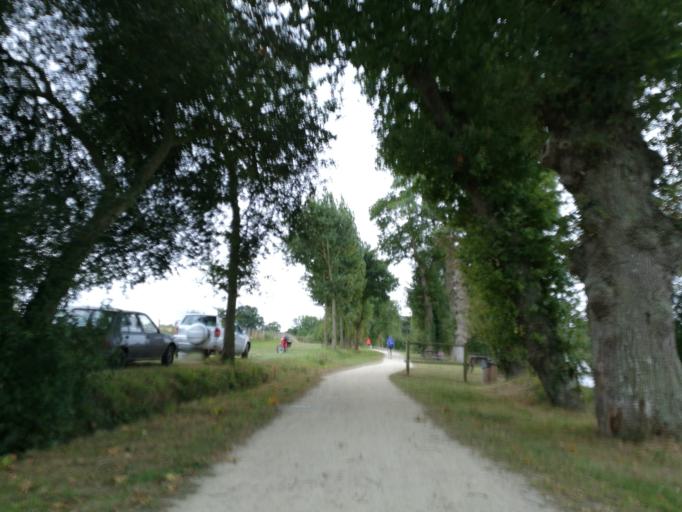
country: FR
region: Brittany
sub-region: Departement d'Ille-et-Vilaine
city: Bedee
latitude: 48.1674
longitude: -1.9536
